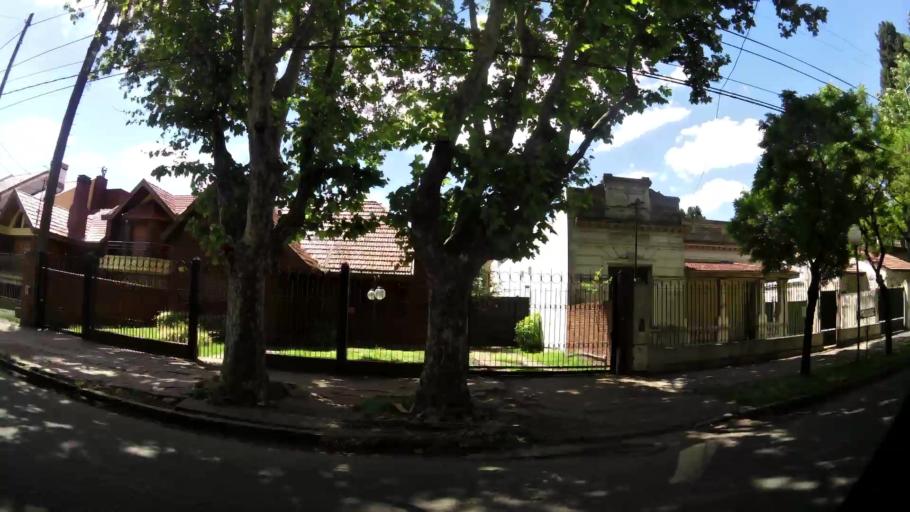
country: AR
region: Buenos Aires
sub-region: Partido de Lomas de Zamora
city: Lomas de Zamora
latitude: -34.7391
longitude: -58.4046
